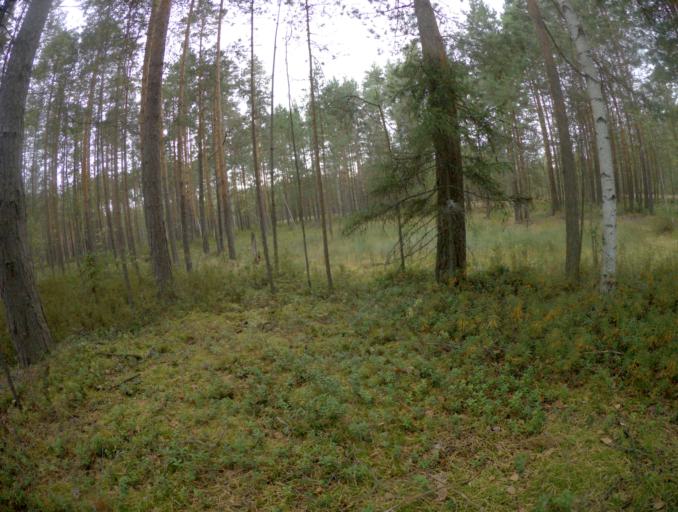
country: RU
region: Vladimir
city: Golovino
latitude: 55.8734
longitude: 40.3989
